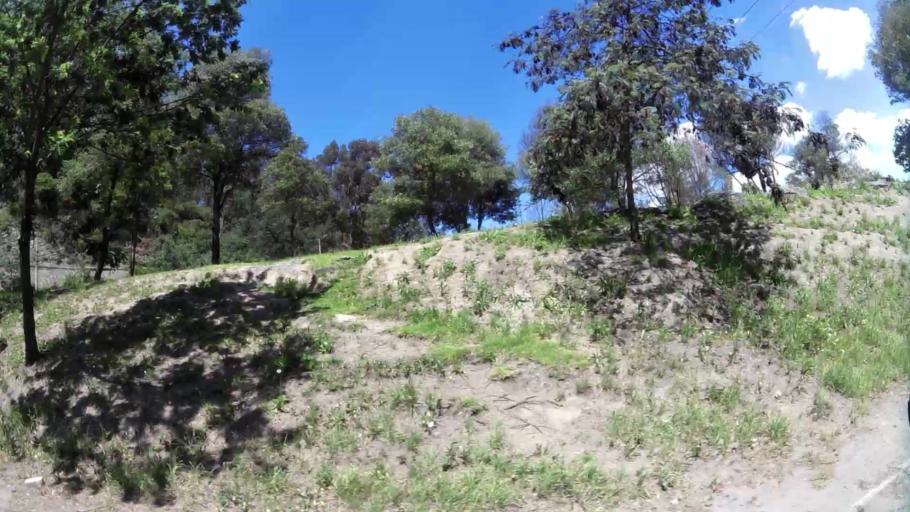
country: EC
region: Pichincha
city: Quito
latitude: -0.0975
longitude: -78.4695
